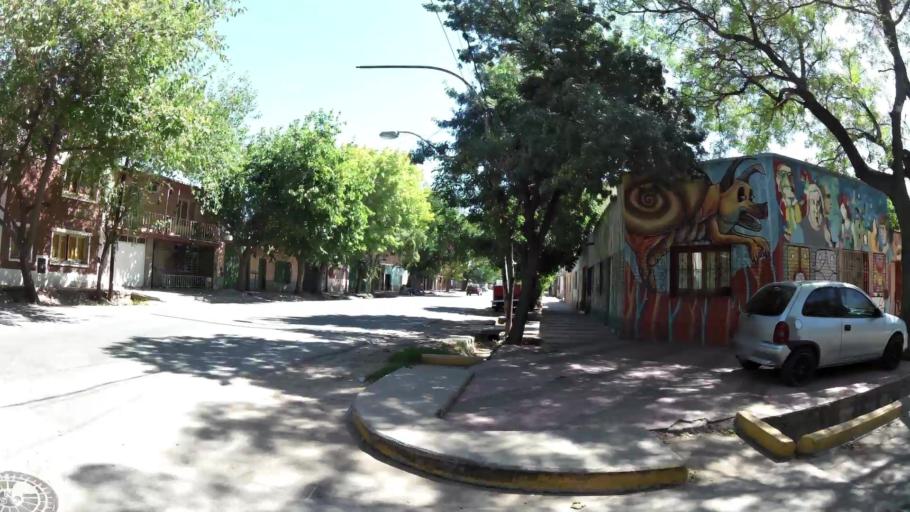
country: AR
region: Mendoza
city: Mendoza
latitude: -32.8842
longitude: -68.8184
